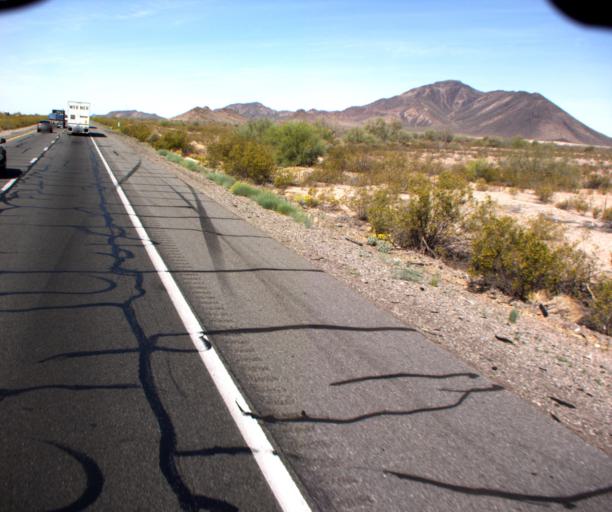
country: US
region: Arizona
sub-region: Maricopa County
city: Buckeye
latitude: 33.5158
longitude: -113.0394
